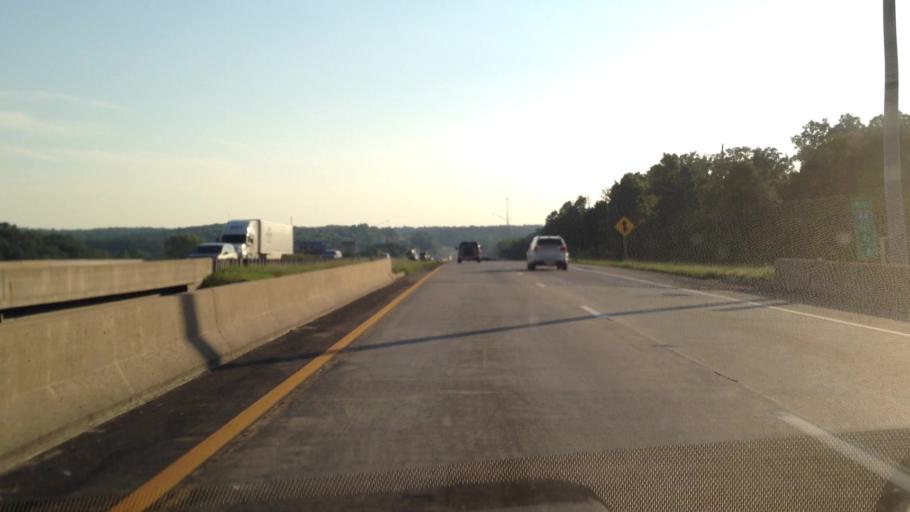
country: US
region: Missouri
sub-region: Jasper County
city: Joplin
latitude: 37.0364
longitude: -94.5149
